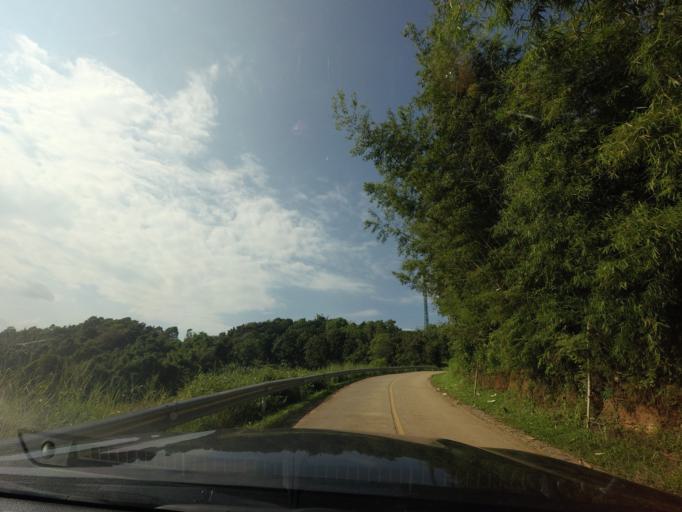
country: TH
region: Nan
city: Na Noi
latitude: 18.3728
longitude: 100.8301
